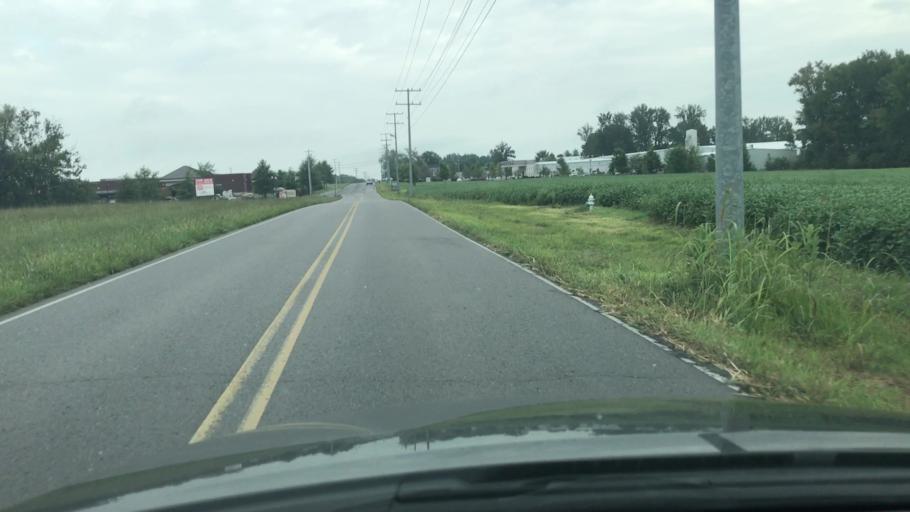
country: US
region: Tennessee
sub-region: Sumner County
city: White House
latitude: 36.4599
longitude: -86.6756
